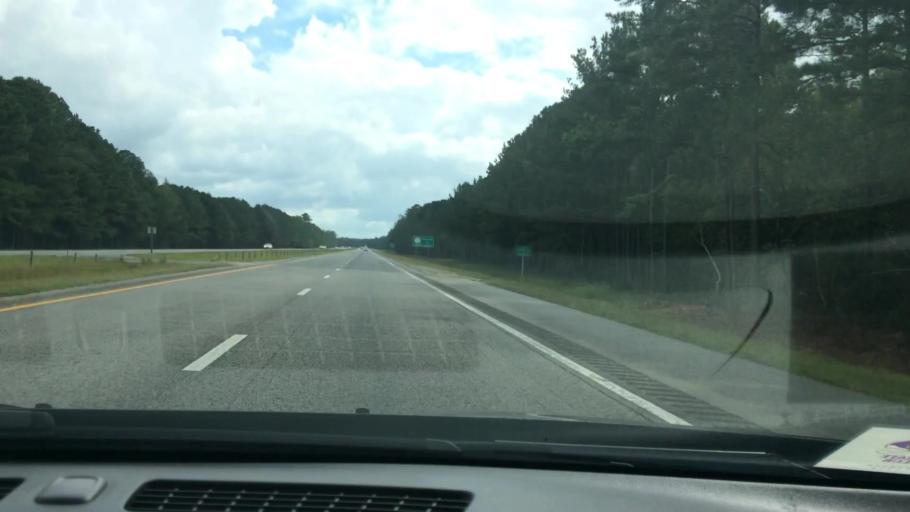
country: US
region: North Carolina
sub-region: Pitt County
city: Farmville
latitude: 35.6366
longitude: -77.7243
